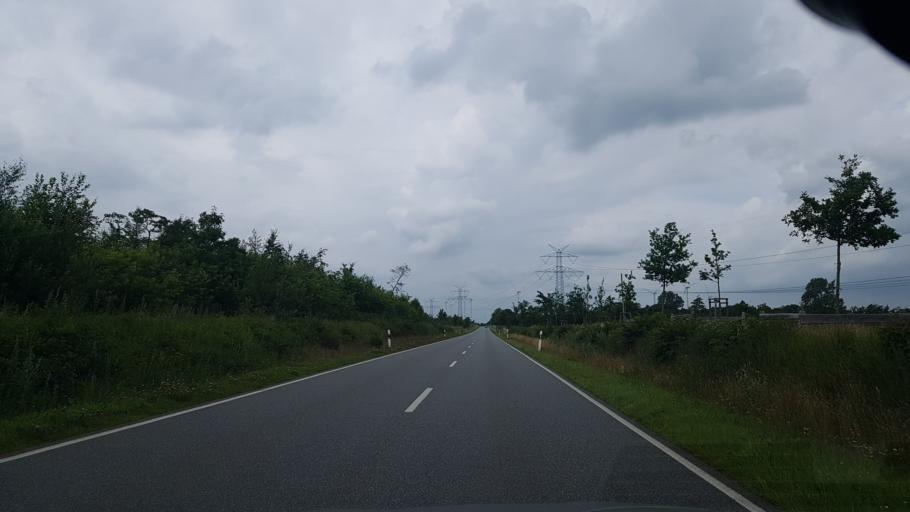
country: DE
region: Schleswig-Holstein
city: Jardelund
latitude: 54.8258
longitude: 9.2194
